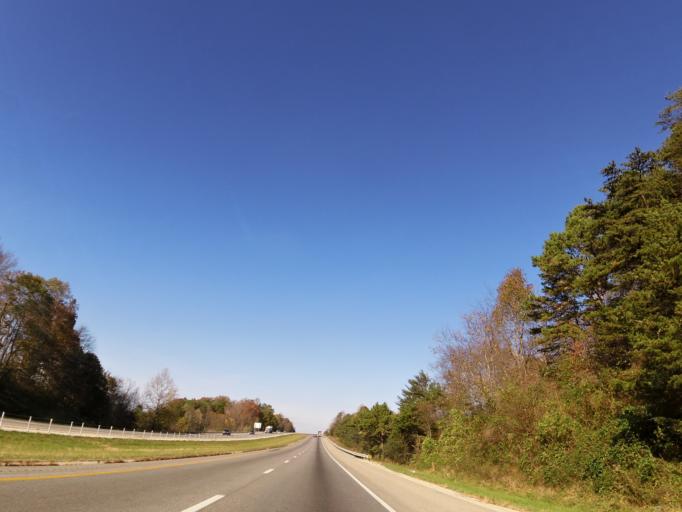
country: US
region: Kentucky
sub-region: Laurel County
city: North Corbin
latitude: 37.0116
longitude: -84.1022
